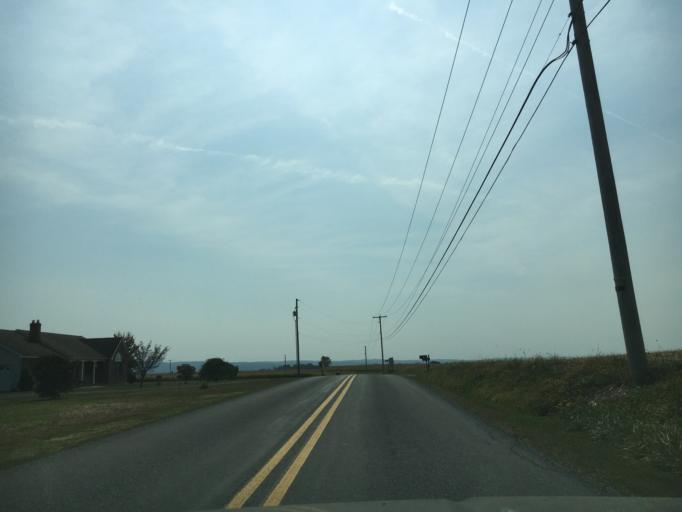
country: US
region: Pennsylvania
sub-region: Berks County
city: Topton
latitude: 40.5611
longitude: -75.7082
